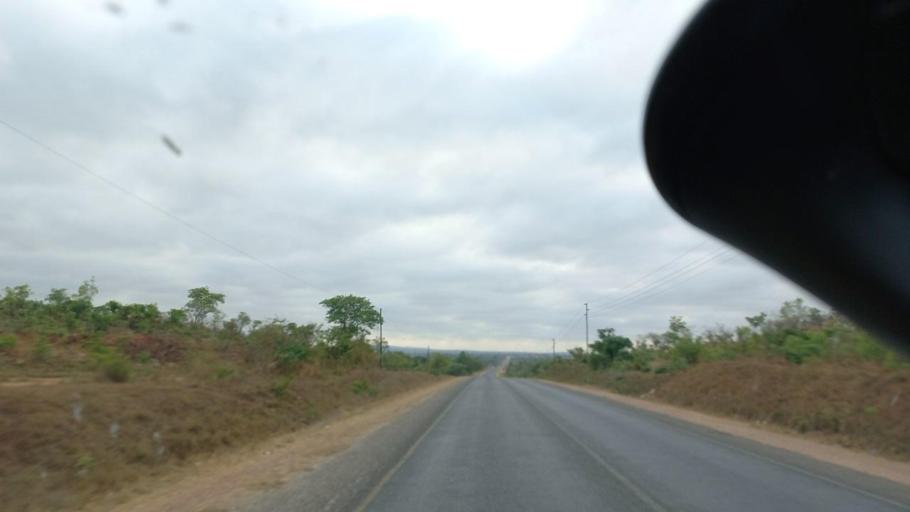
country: ZM
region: Lusaka
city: Chongwe
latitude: -15.3414
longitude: 28.6042
